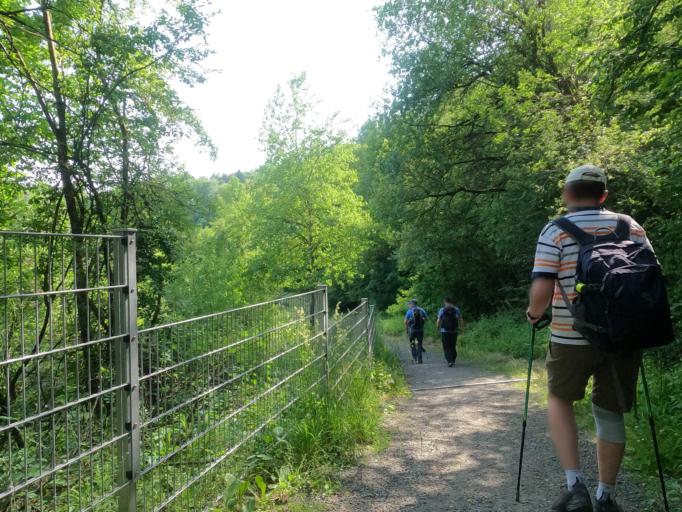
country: DE
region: Rheinland-Pfalz
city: Bad Marienberg
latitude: 50.6476
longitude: 7.9360
